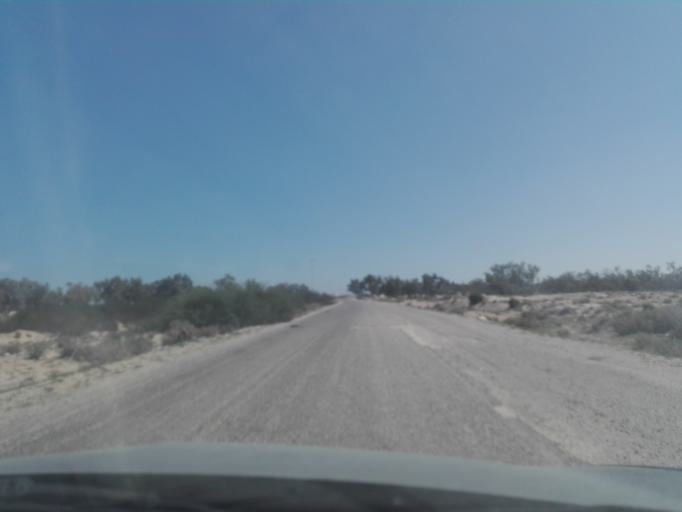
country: TN
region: Qabis
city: Gabes
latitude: 33.8720
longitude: 10.0359
